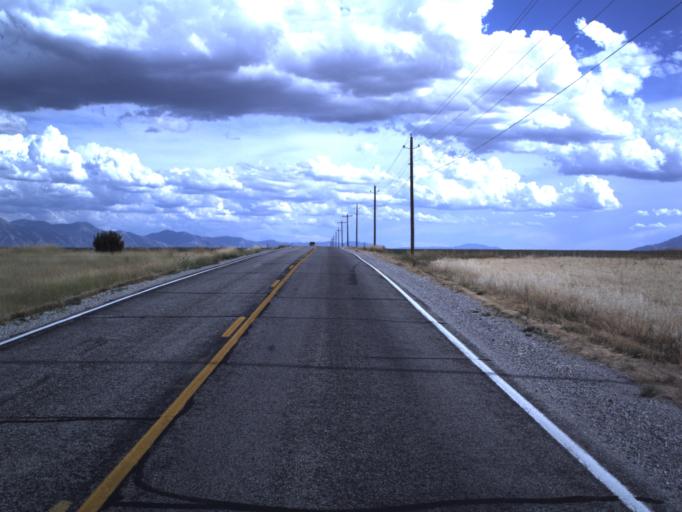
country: US
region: Utah
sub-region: Cache County
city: Benson
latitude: 41.8960
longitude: -112.0437
